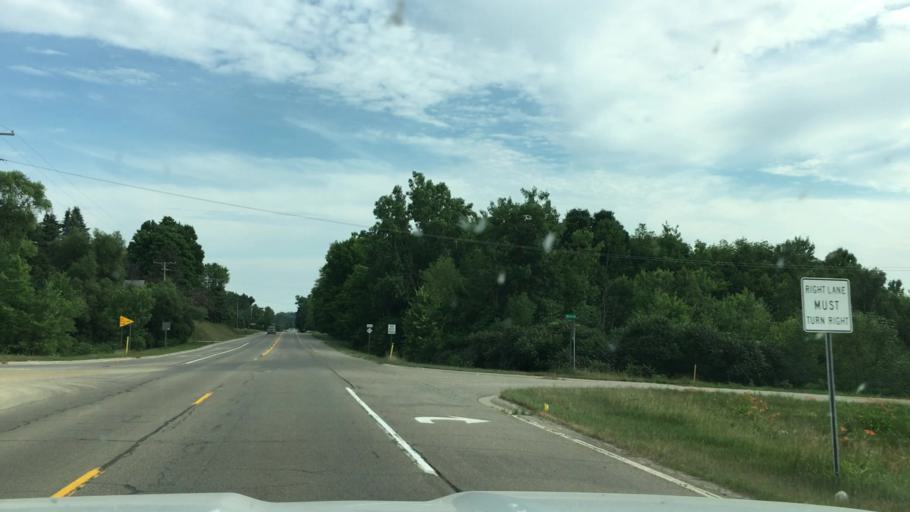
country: US
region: Michigan
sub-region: Sanilac County
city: Brown City
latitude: 43.1675
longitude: -83.0758
